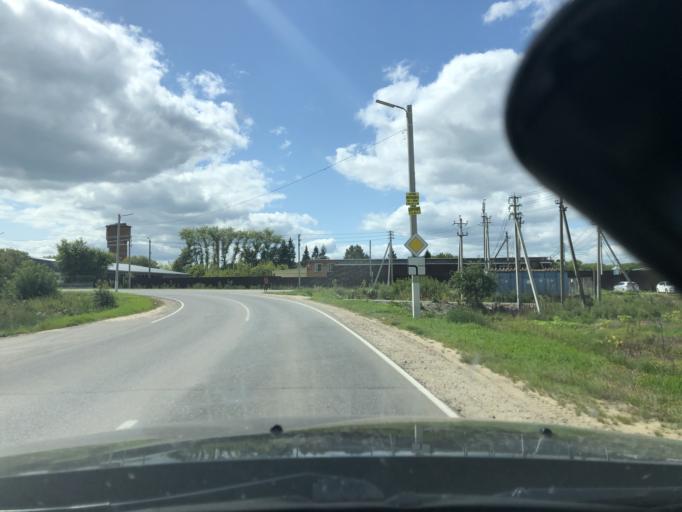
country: RU
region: Tula
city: Gorelki
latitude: 54.3408
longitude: 37.5644
